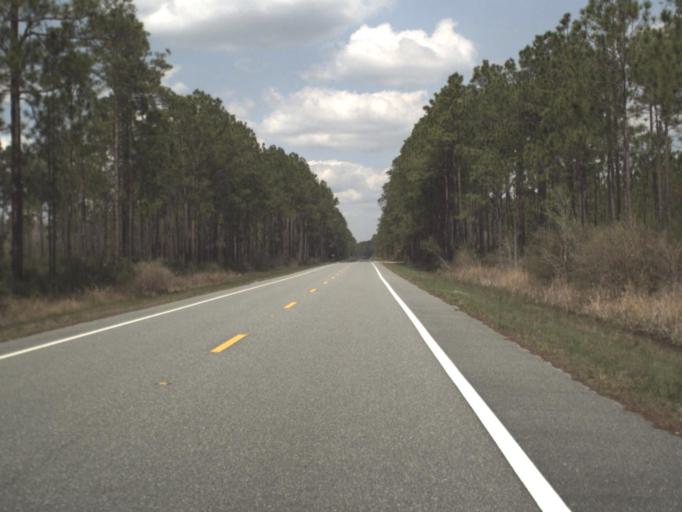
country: US
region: Florida
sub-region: Franklin County
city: Apalachicola
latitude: 29.8837
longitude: -84.9765
